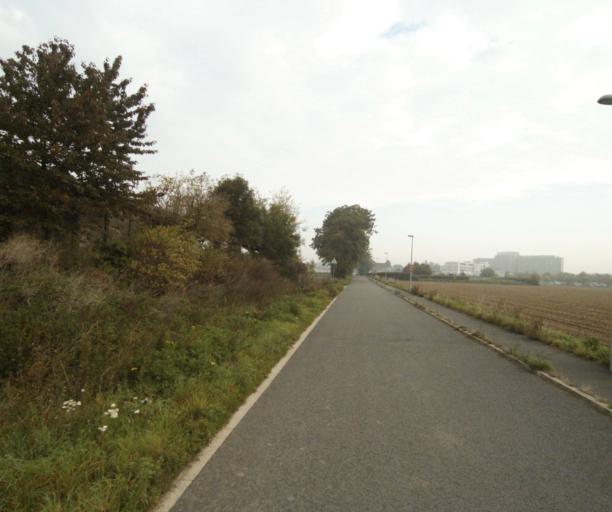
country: FR
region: Nord-Pas-de-Calais
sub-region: Departement du Nord
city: Seclin
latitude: 50.5447
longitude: 3.0116
